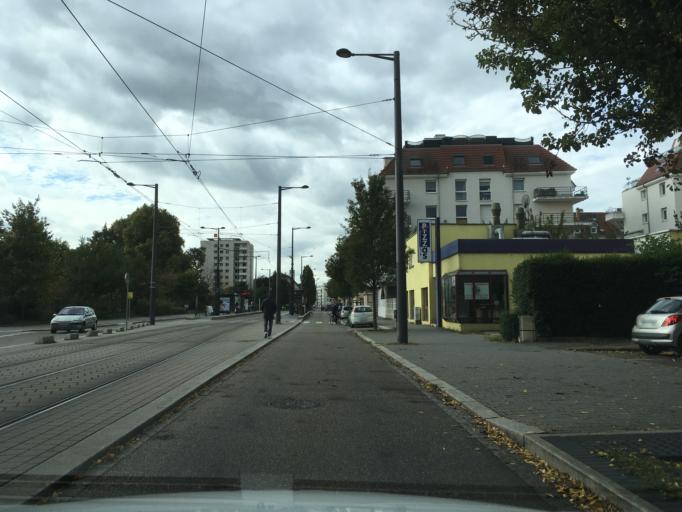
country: FR
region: Alsace
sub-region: Departement du Bas-Rhin
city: Strasbourg
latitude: 48.5650
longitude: 7.7704
